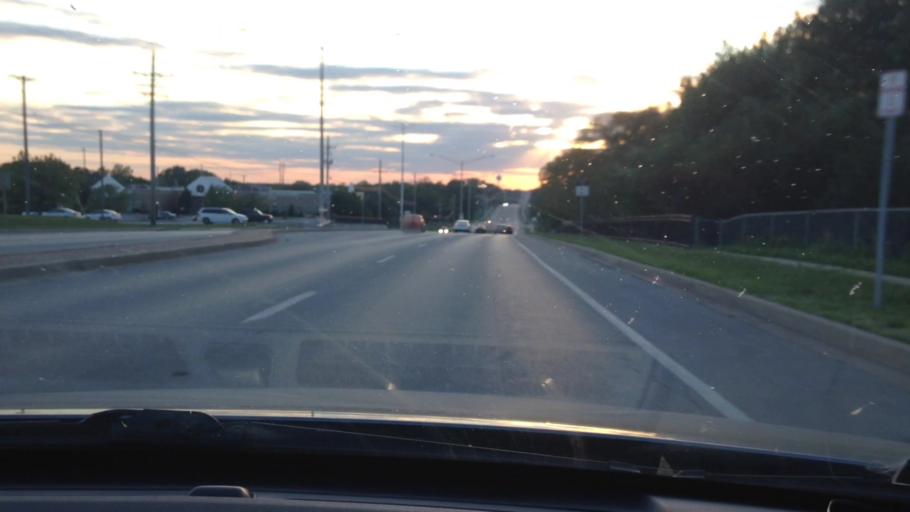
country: US
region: Missouri
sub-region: Platte County
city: Weatherby Lake
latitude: 39.2470
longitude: -94.6699
